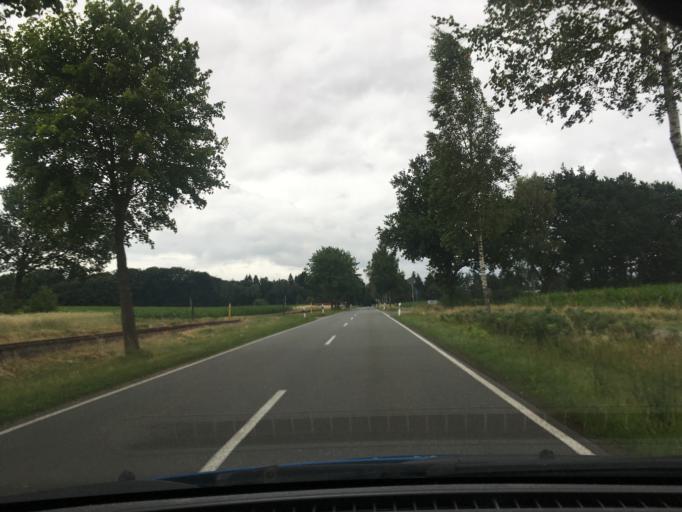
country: DE
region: Lower Saxony
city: Toppenstedt
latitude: 53.2804
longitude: 10.1293
